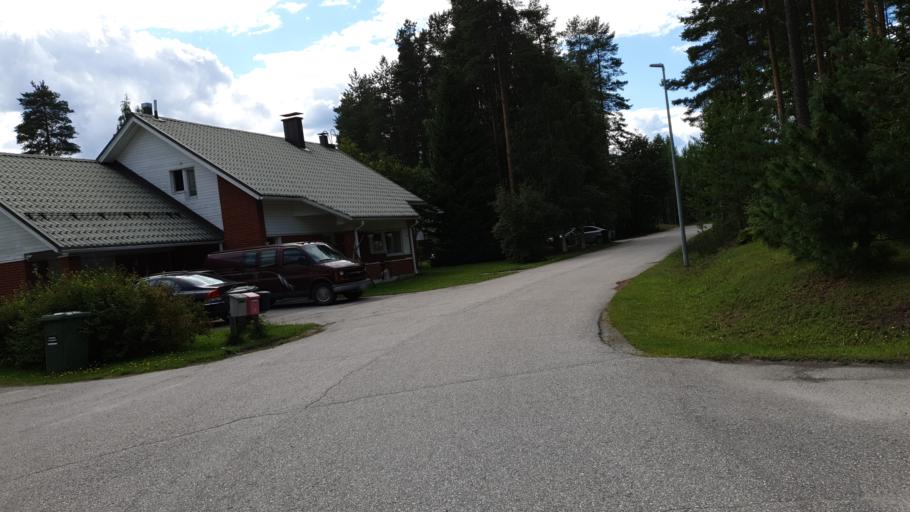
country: FI
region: Kainuu
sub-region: Kehys-Kainuu
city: Kuhmo
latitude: 64.1258
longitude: 29.5562
